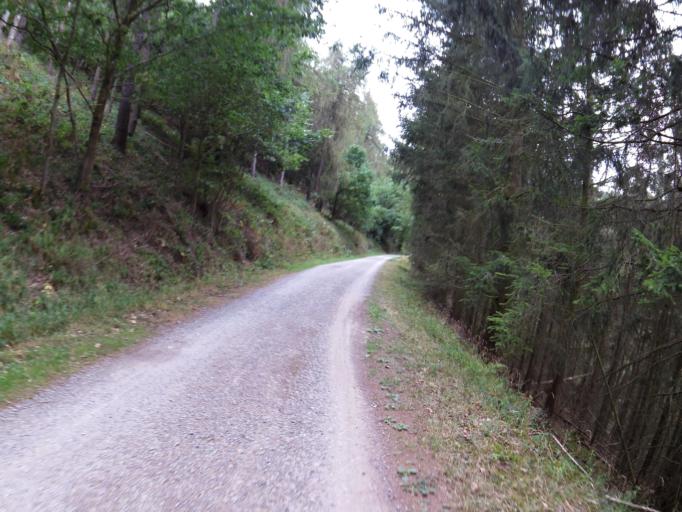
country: DE
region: North Rhine-Westphalia
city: Heimbach
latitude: 50.6330
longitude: 6.4224
